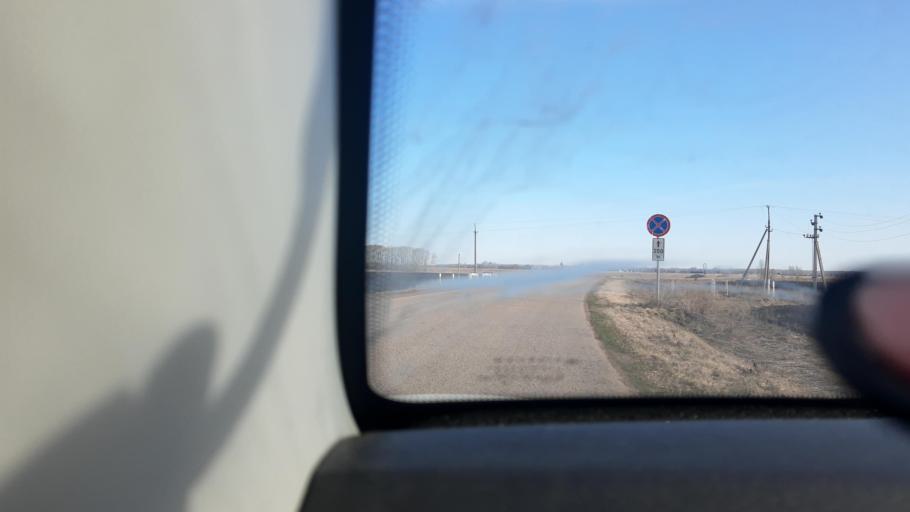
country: RU
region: Bashkortostan
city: Asanovo
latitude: 54.9382
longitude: 55.5193
